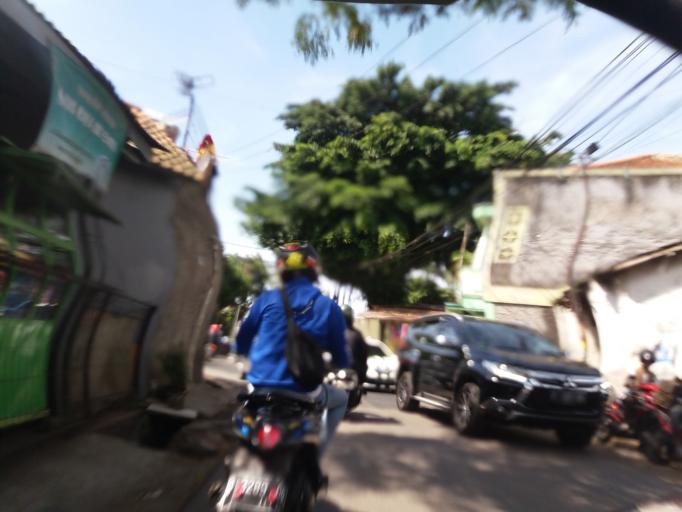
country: ID
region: West Java
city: Margahayukencana
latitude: -6.9529
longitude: 107.5807
